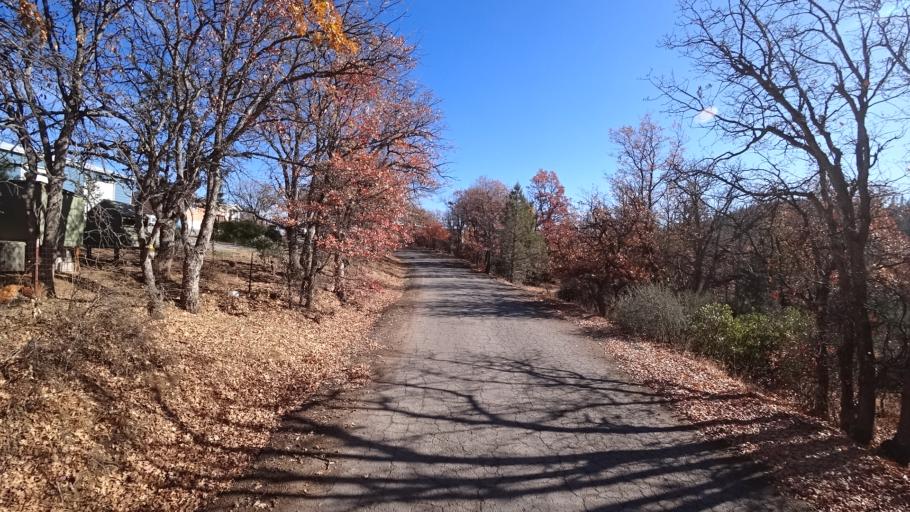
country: US
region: California
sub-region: Siskiyou County
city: Yreka
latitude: 41.7732
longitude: -122.6461
